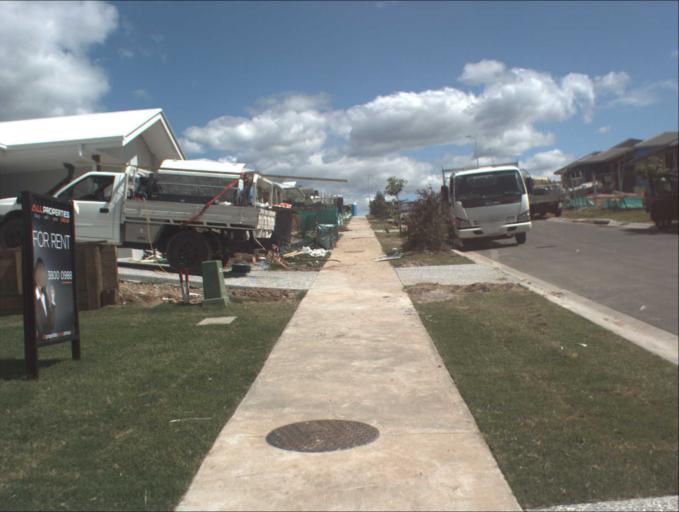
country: AU
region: Queensland
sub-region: Logan
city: Chambers Flat
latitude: -27.8020
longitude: 153.1163
